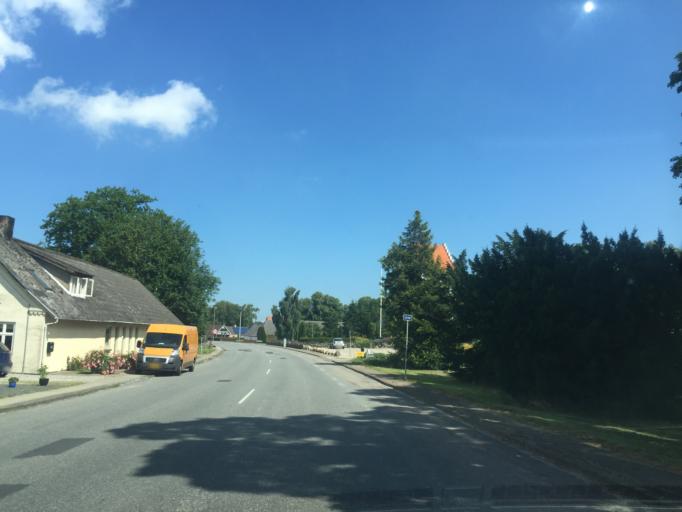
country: DK
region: South Denmark
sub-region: Nordfyns Kommune
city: Otterup
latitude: 55.5430
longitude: 10.3911
